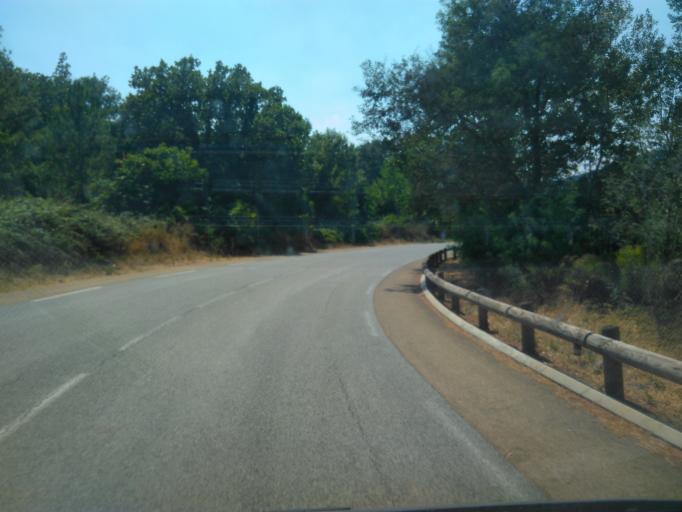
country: FR
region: Provence-Alpes-Cote d'Azur
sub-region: Departement du Var
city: La Garde-Freinet
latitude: 43.3017
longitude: 6.4824
